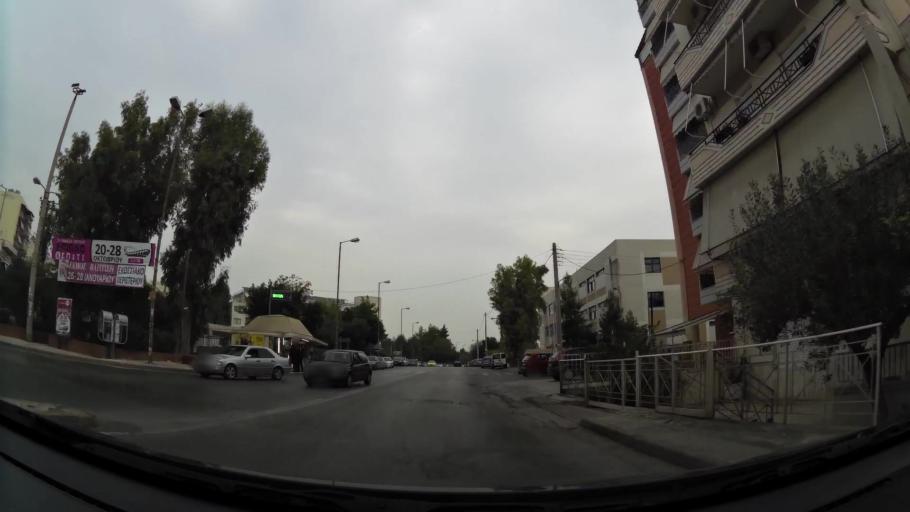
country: GR
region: Attica
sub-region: Nomos Piraios
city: Agios Ioannis Rentis
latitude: 37.9703
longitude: 23.6617
